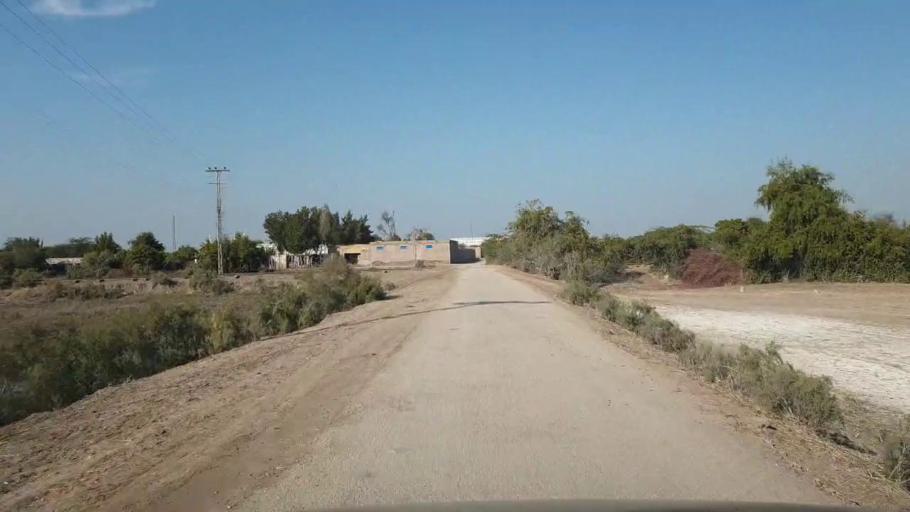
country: PK
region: Sindh
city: Shahpur Chakar
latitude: 26.1549
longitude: 68.6839
